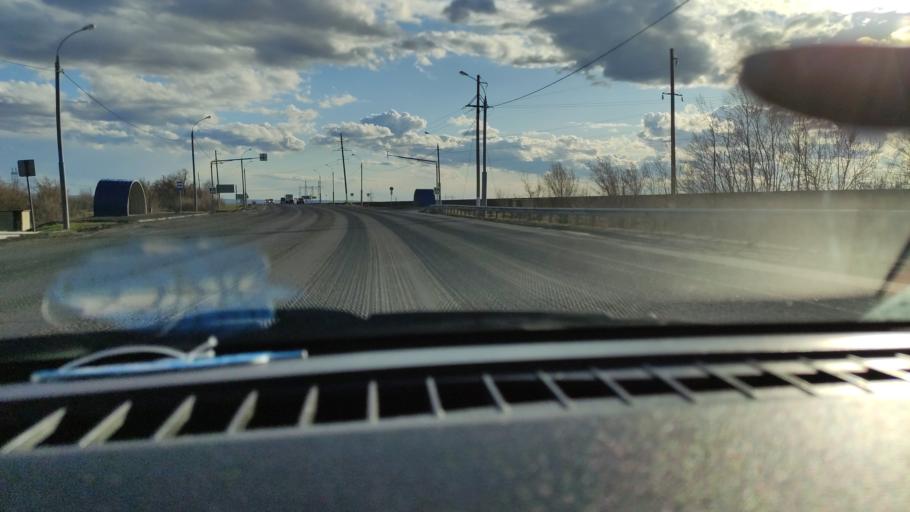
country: RU
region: Saratov
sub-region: Saratovskiy Rayon
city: Saratov
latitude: 51.7691
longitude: 46.0812
